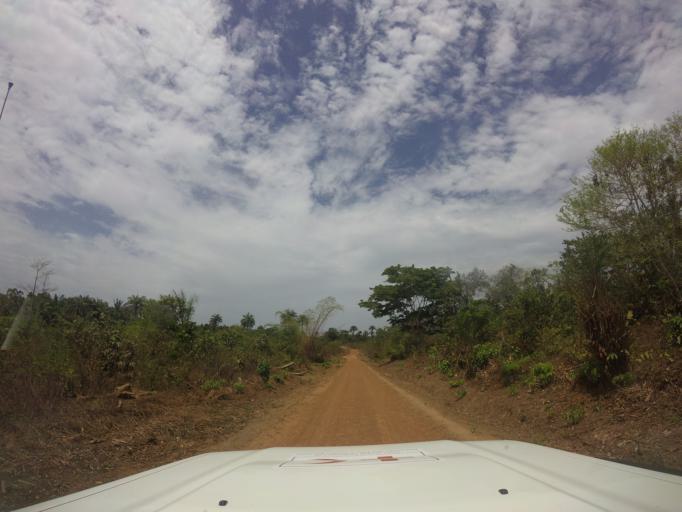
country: SL
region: Southern Province
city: Zimmi
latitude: 7.1399
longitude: -11.2795
